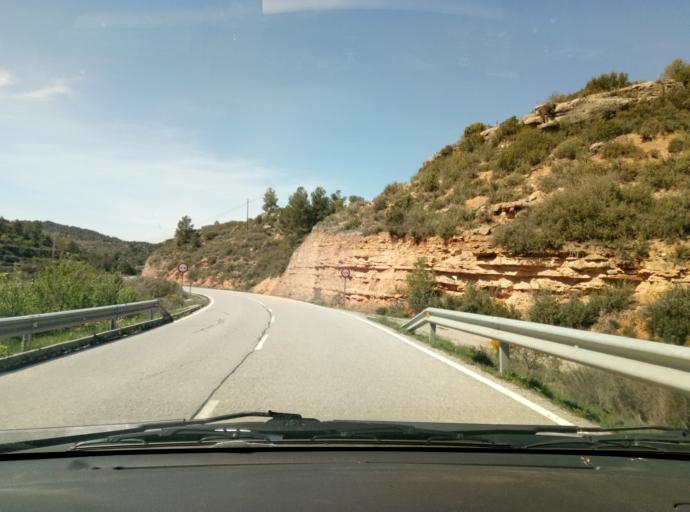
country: ES
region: Catalonia
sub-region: Provincia de Tarragona
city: Ulldemolins
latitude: 41.4256
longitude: 0.8698
